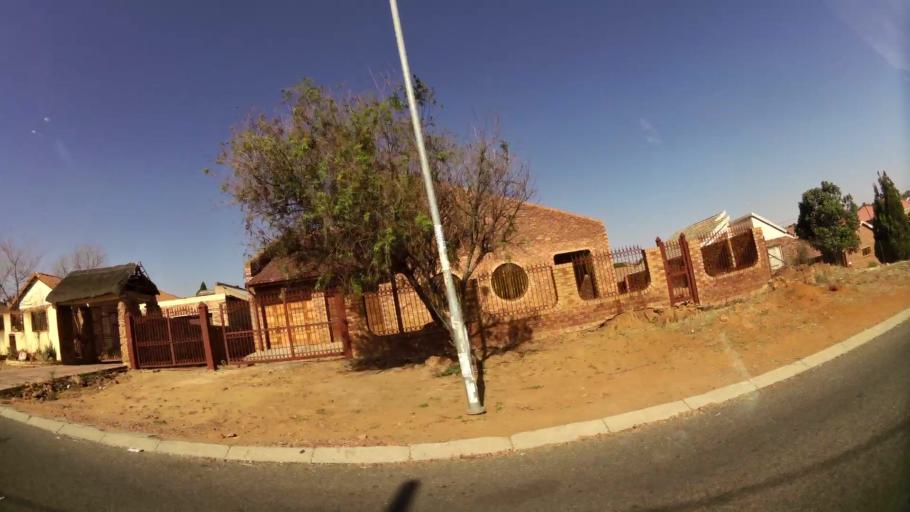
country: ZA
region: Gauteng
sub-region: City of Tshwane Metropolitan Municipality
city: Mabopane
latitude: -25.5281
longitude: 28.0942
